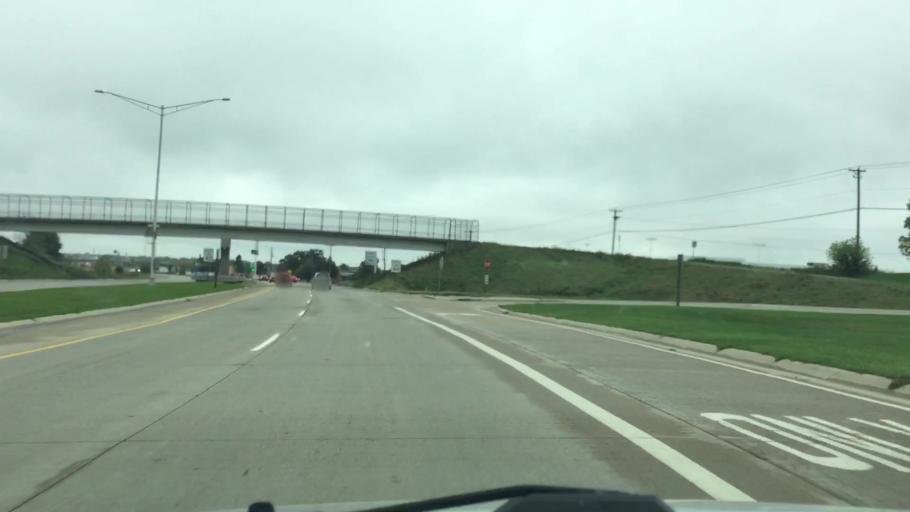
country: US
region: Wisconsin
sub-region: Rock County
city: Janesville
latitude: 42.7331
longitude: -88.9877
